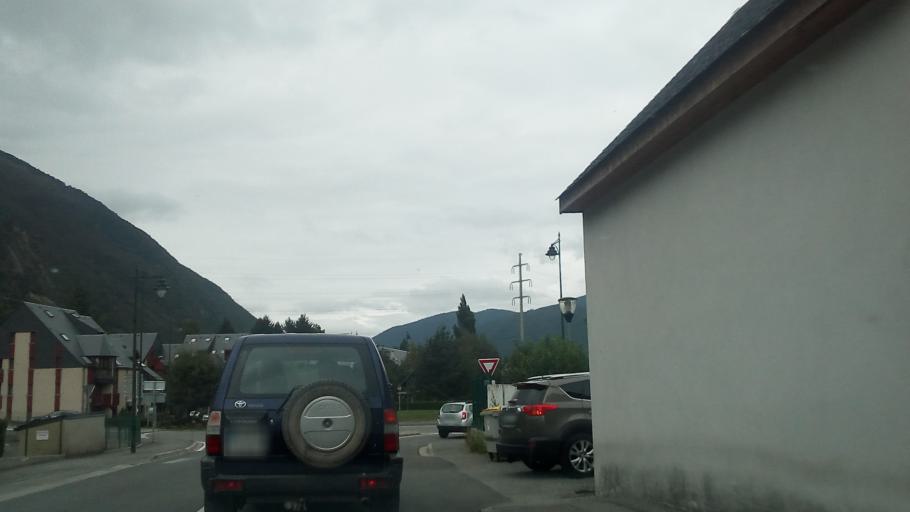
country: FR
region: Midi-Pyrenees
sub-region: Departement des Hautes-Pyrenees
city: Saint-Lary-Soulan
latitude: 42.8227
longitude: 0.3235
